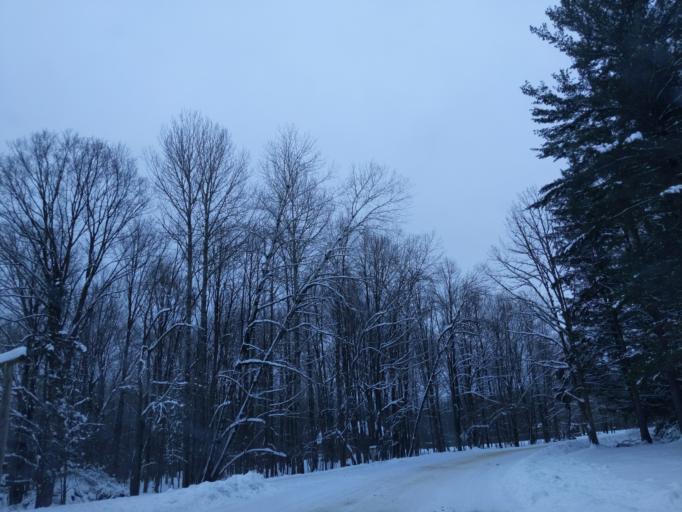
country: US
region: Wisconsin
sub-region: Marathon County
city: Marathon
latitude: 44.7716
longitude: -89.8681
